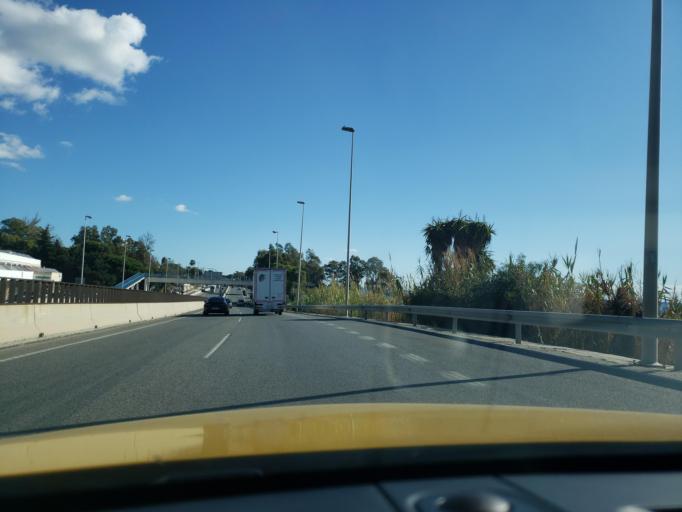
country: ES
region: Andalusia
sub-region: Provincia de Malaga
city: Marbella
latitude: 36.5086
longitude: -4.8597
